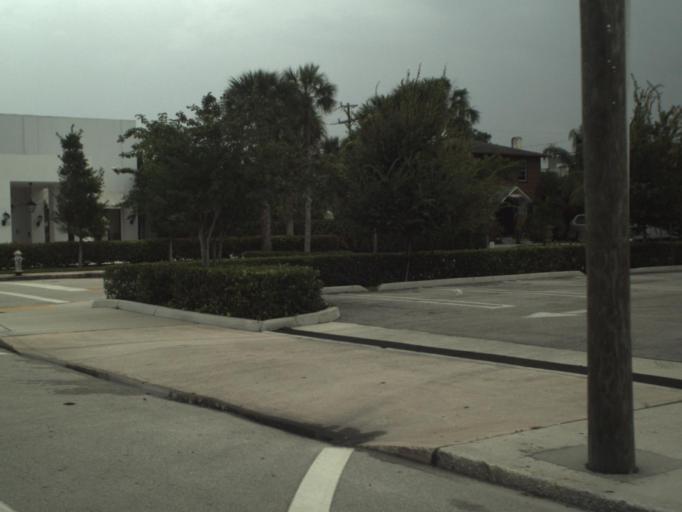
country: US
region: Florida
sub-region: Palm Beach County
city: Palm Beach
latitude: 26.6814
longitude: -80.0547
